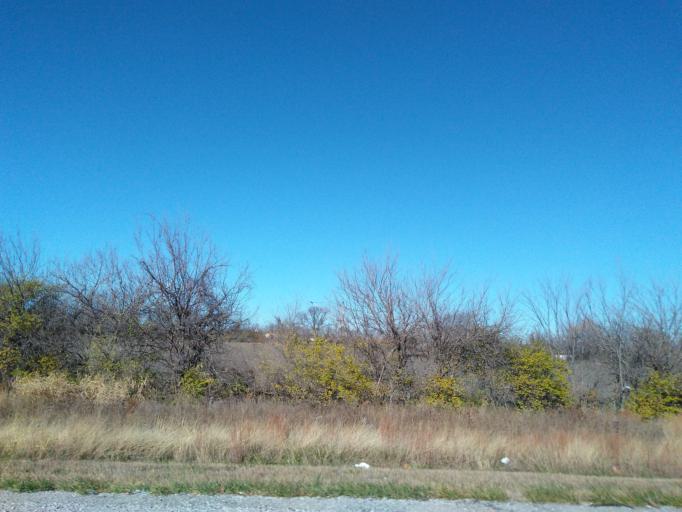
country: US
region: Illinois
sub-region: Saint Clair County
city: Cahokia
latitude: 38.5416
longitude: -90.1777
